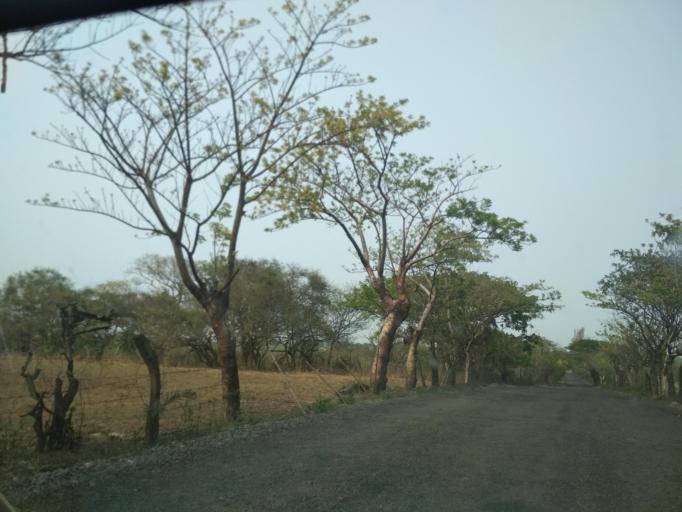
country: MX
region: Veracruz
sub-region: Veracruz
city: Delfino Victoria (Santa Fe)
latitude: 19.1565
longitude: -96.2686
